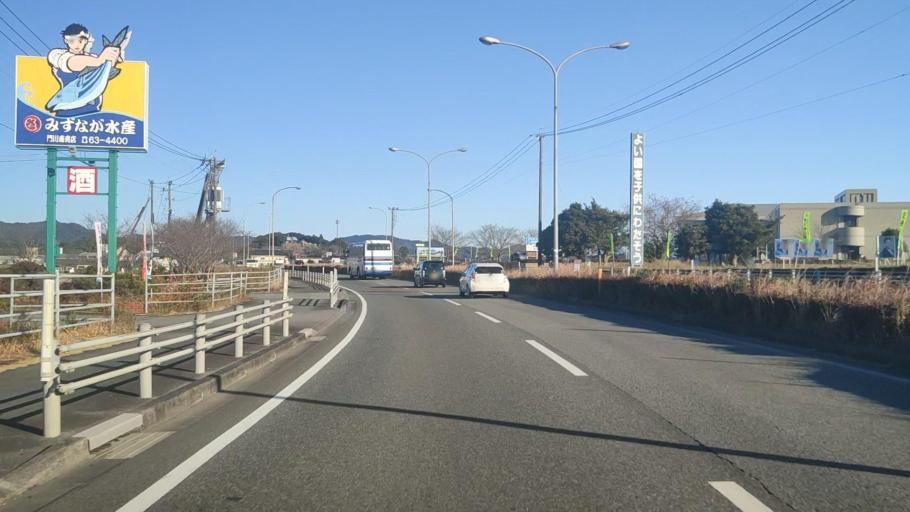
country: JP
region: Miyazaki
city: Nobeoka
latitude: 32.4626
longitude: 131.6488
